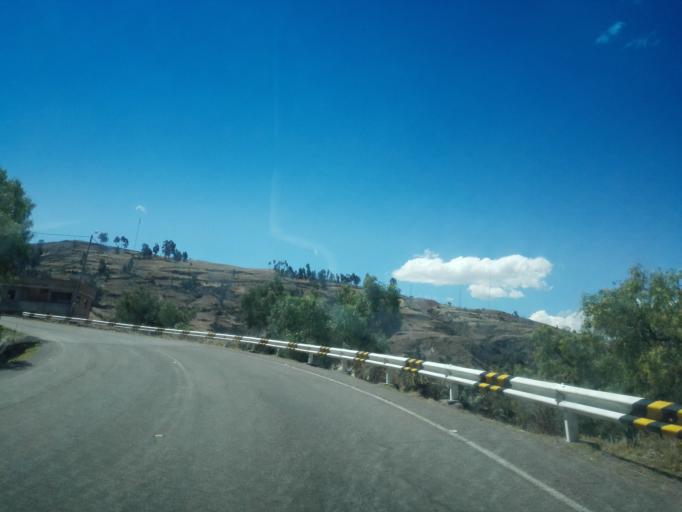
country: PE
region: Ayacucho
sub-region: Provincia de Huamanga
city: Ayacucho
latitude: -13.1664
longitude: -74.2446
